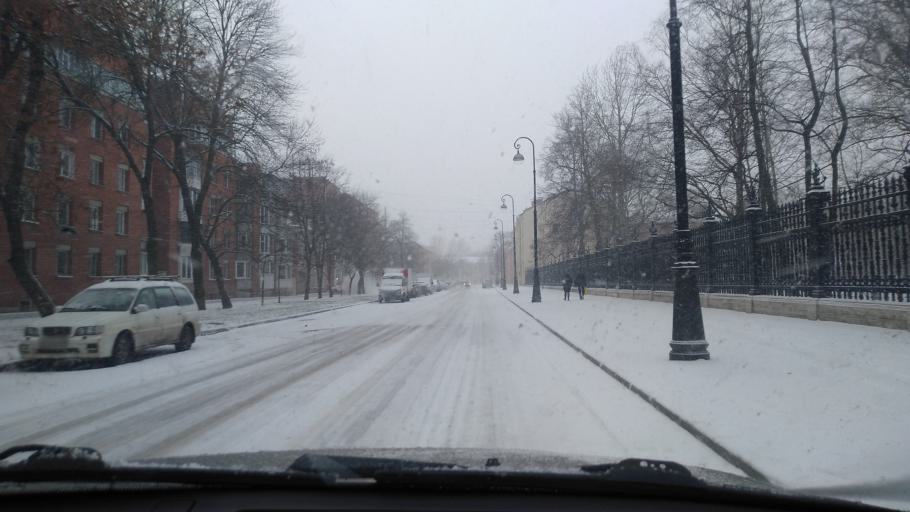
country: RU
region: St.-Petersburg
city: Kronshtadt
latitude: 59.9873
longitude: 29.7772
